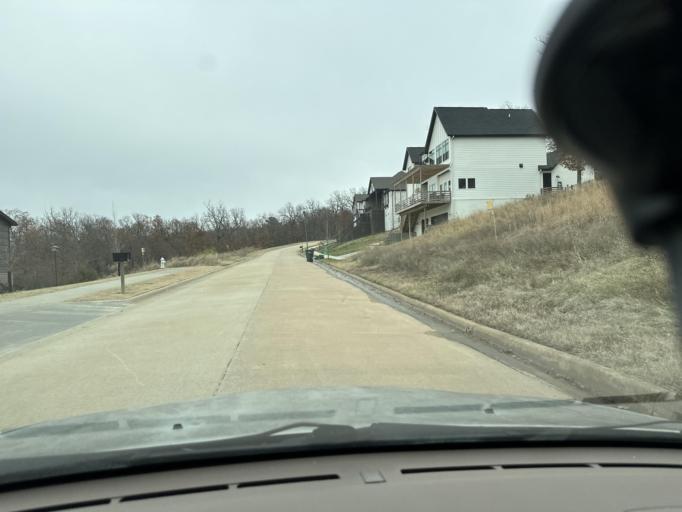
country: US
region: Arkansas
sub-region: Washington County
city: Fayetteville
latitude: 36.0927
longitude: -94.1499
